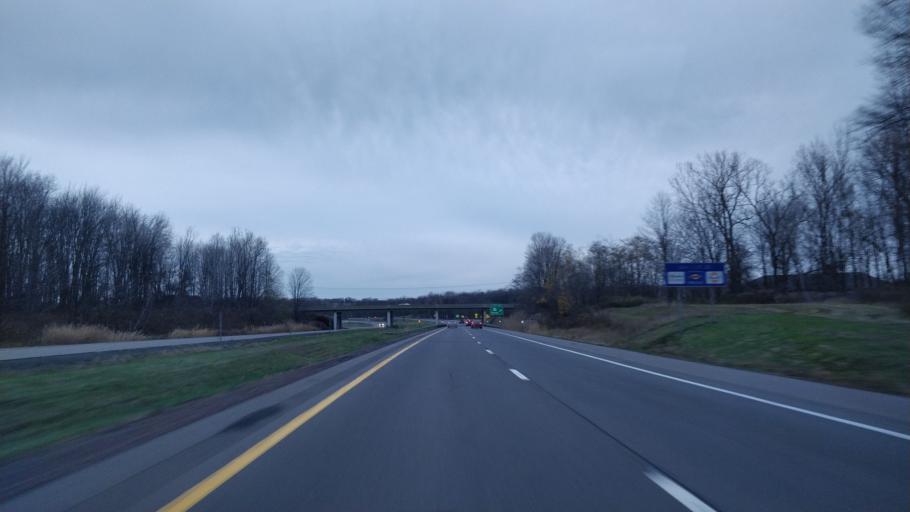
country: US
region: New York
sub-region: Oswego County
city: Central Square
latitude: 43.4019
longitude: -76.1177
